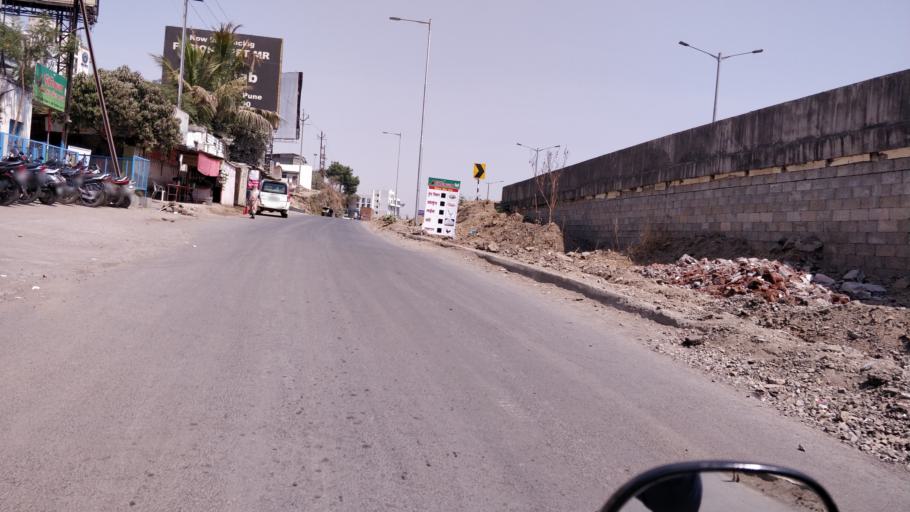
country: IN
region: Maharashtra
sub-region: Pune Division
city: Kharakvasla
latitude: 18.5162
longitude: 73.7688
